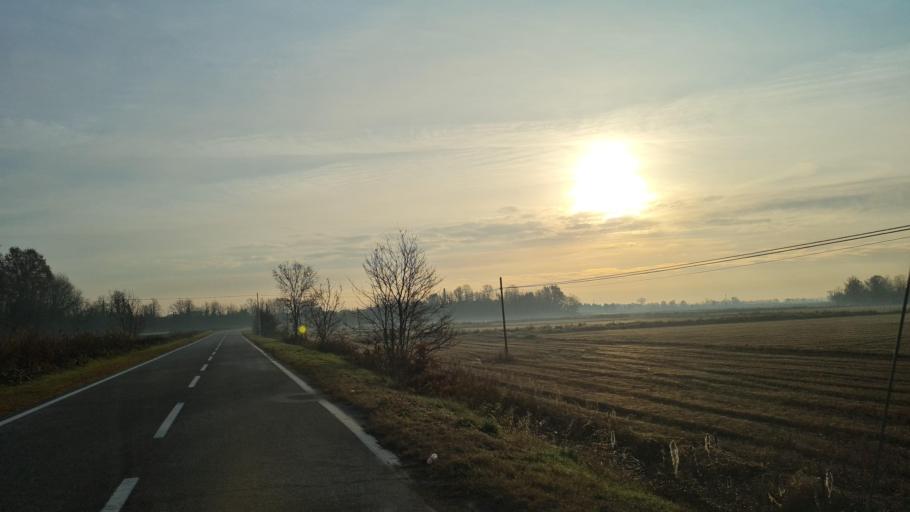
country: IT
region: Piedmont
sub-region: Provincia di Vercelli
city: Villarboit
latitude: 45.4417
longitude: 8.3246
